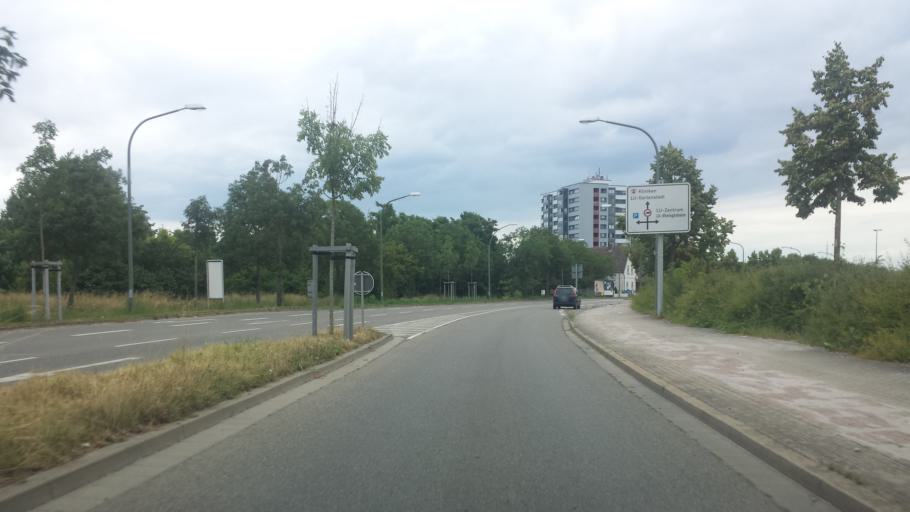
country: DE
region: Rheinland-Pfalz
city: Gartenstadt
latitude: 49.4550
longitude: 8.3924
